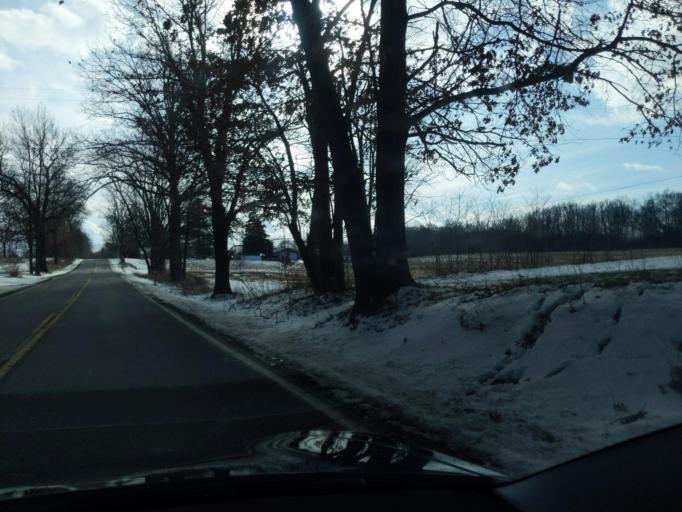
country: US
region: Michigan
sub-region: Ingham County
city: Stockbridge
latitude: 42.4523
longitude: -84.0763
